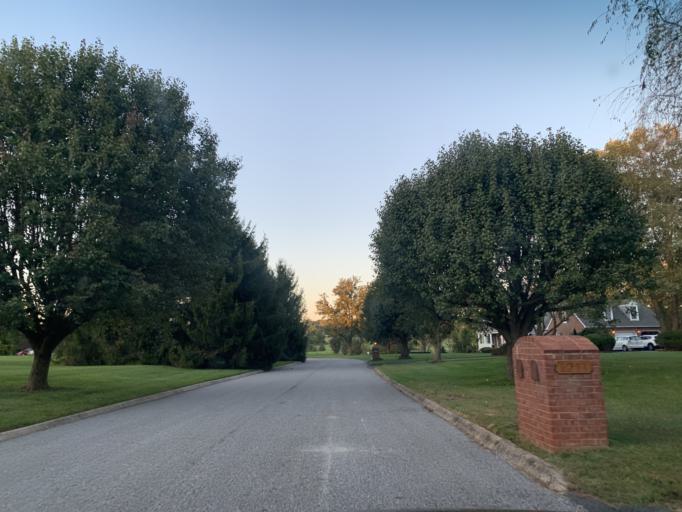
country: US
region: Maryland
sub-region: Harford County
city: Bel Air South
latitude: 39.5158
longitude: -76.2883
